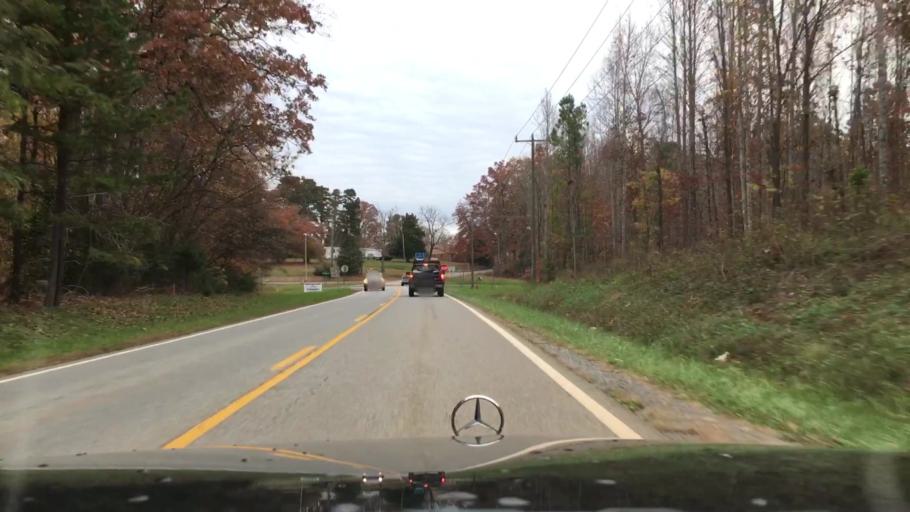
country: US
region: Virginia
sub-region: Campbell County
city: Timberlake
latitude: 37.2315
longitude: -79.2815
